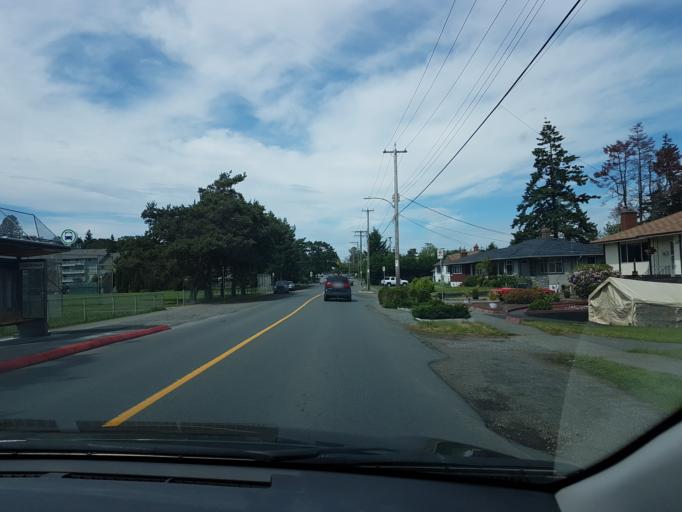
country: CA
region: British Columbia
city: Oak Bay
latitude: 48.4665
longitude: -123.3359
